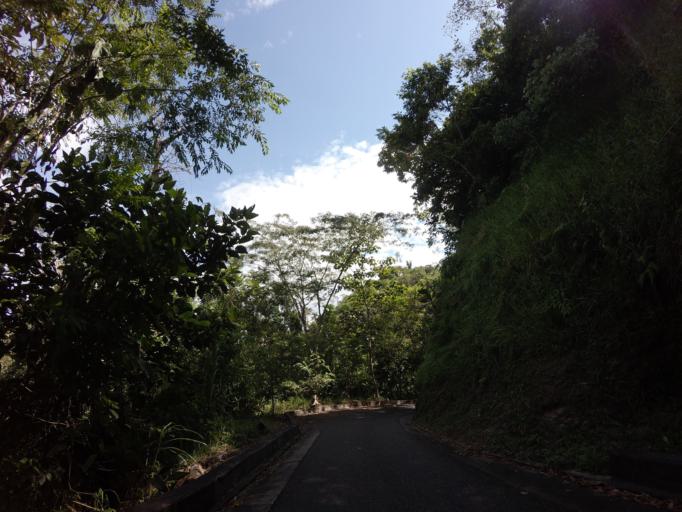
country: CO
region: Caldas
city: Norcasia
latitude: 5.5694
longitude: -74.9039
